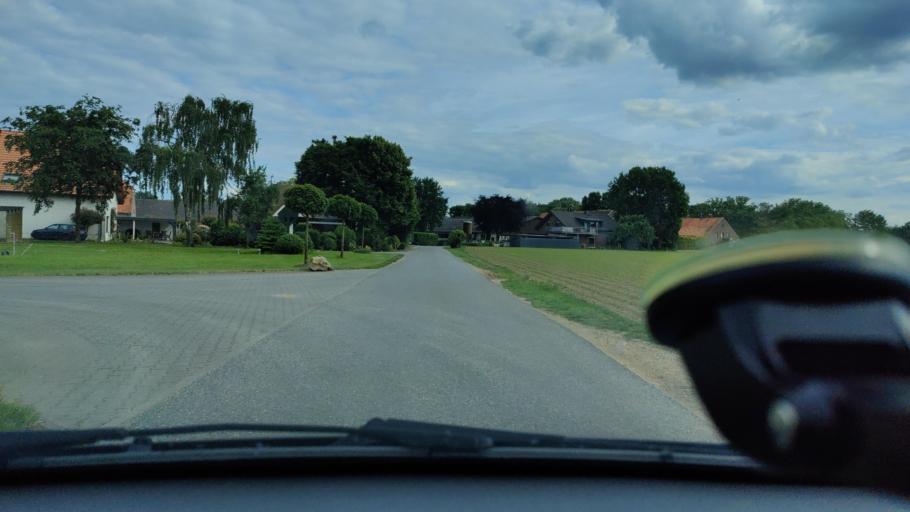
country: DE
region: North Rhine-Westphalia
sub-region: Regierungsbezirk Dusseldorf
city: Weeze
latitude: 51.6565
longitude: 6.1919
